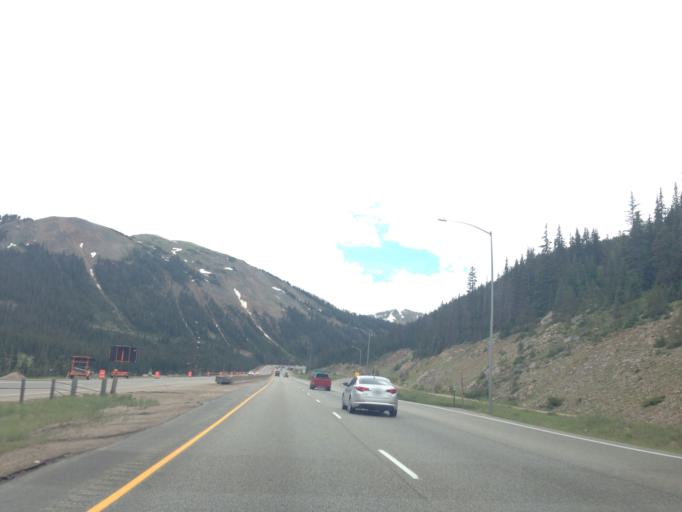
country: US
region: Colorado
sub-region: Summit County
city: Keystone
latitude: 39.6891
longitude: -105.8821
